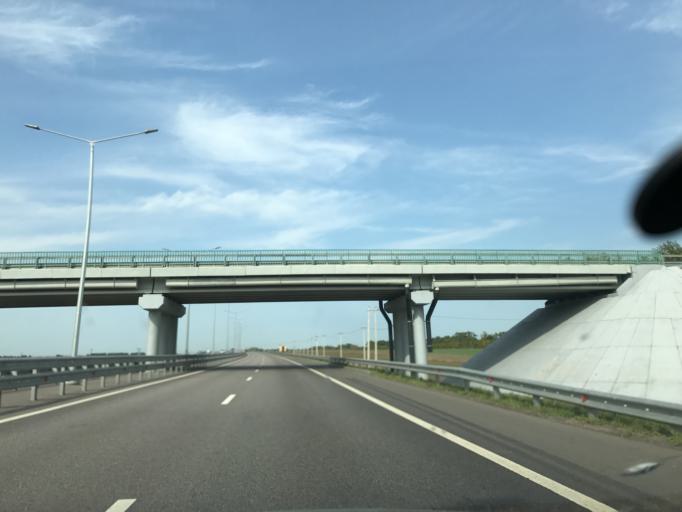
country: RU
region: Voronezj
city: Podkletnoye
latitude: 51.5334
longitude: 39.5074
